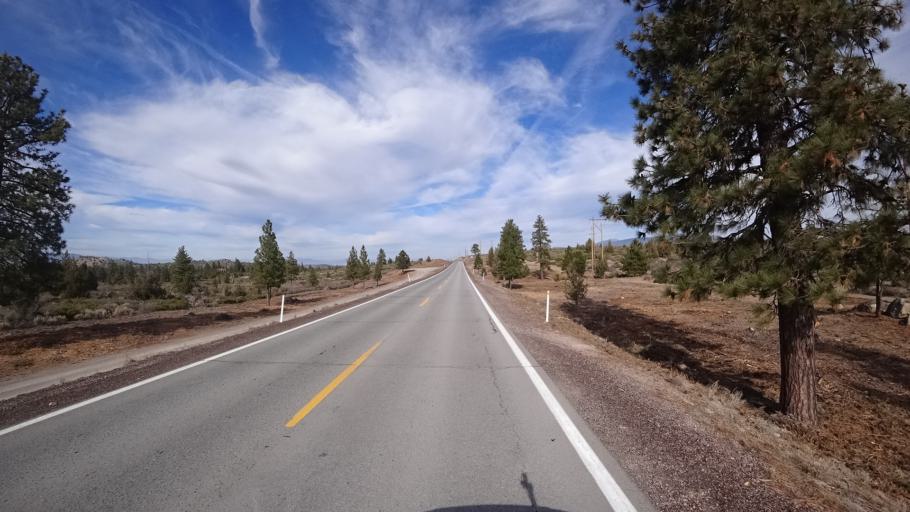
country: US
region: California
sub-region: Siskiyou County
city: Weed
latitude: 41.4886
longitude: -122.3623
